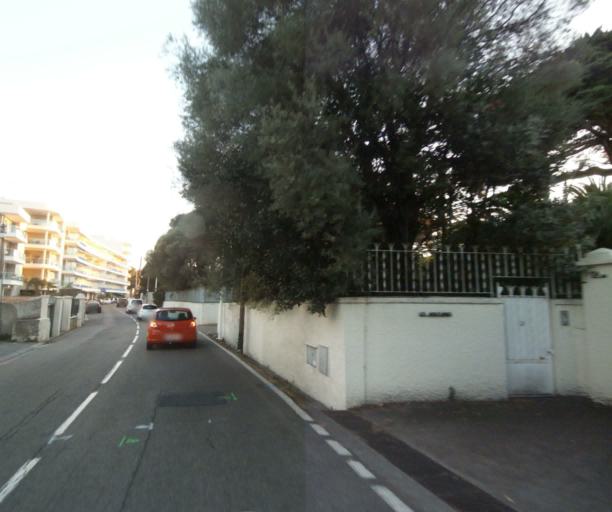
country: FR
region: Provence-Alpes-Cote d'Azur
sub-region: Departement des Alpes-Maritimes
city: Antibes
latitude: 43.5544
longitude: 7.1285
